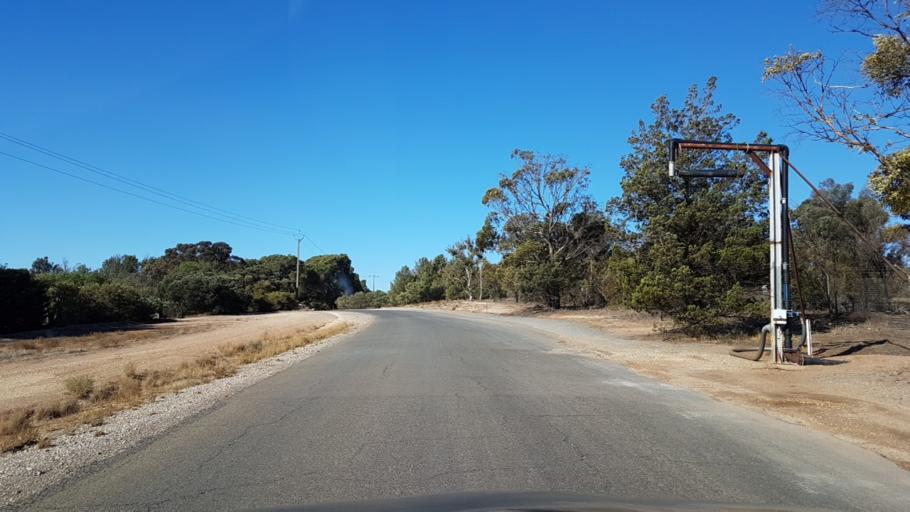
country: AU
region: South Australia
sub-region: Clare and Gilbert Valleys
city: Clare
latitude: -33.6756
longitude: 138.9196
